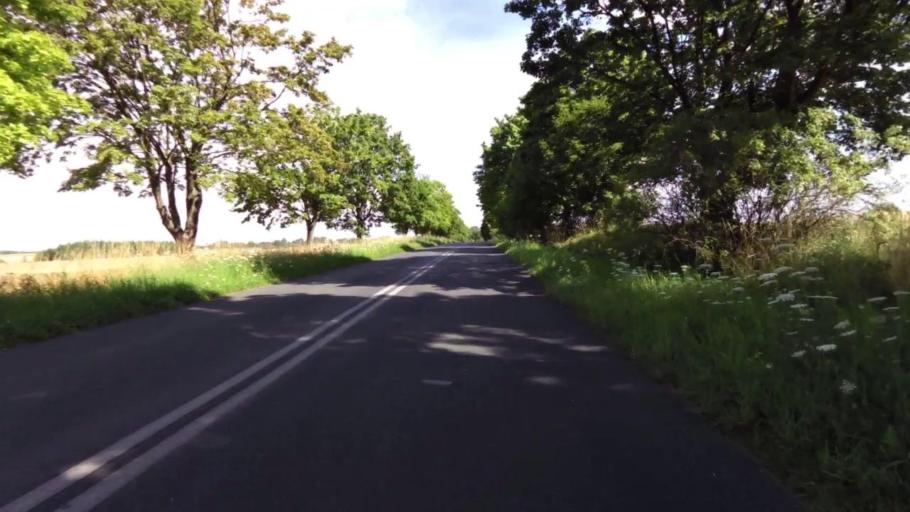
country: PL
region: West Pomeranian Voivodeship
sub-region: Powiat stargardzki
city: Dobrzany
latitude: 53.3983
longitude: 15.4309
